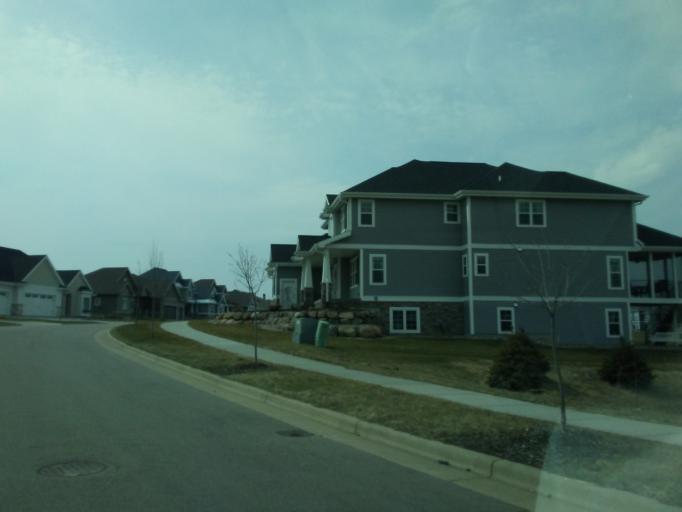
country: US
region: Wisconsin
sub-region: Dane County
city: Waunakee
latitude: 43.1702
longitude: -89.4488
